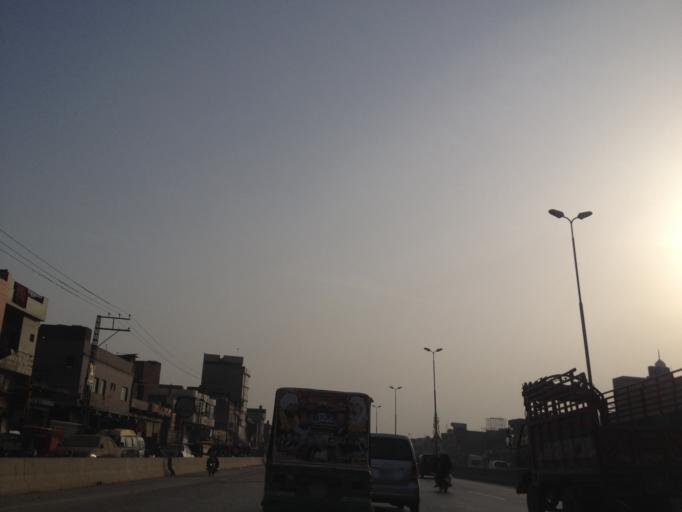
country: PK
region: Punjab
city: Lahore
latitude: 31.5646
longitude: 74.2807
